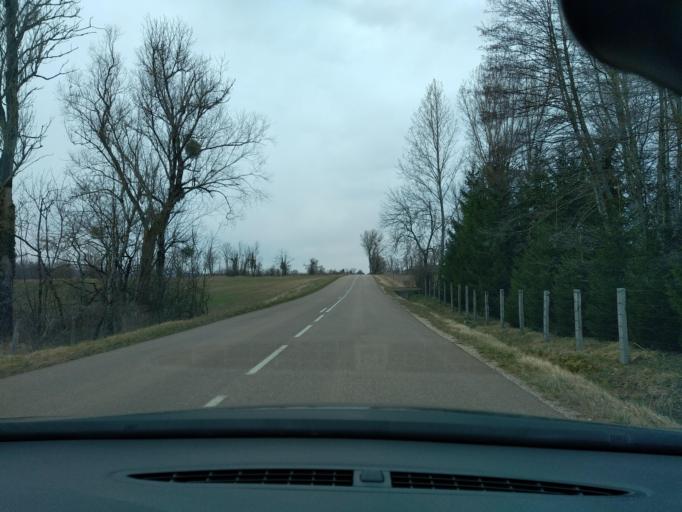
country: FR
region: Franche-Comte
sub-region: Departement du Jura
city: Arinthod
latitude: 46.3719
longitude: 5.5617
